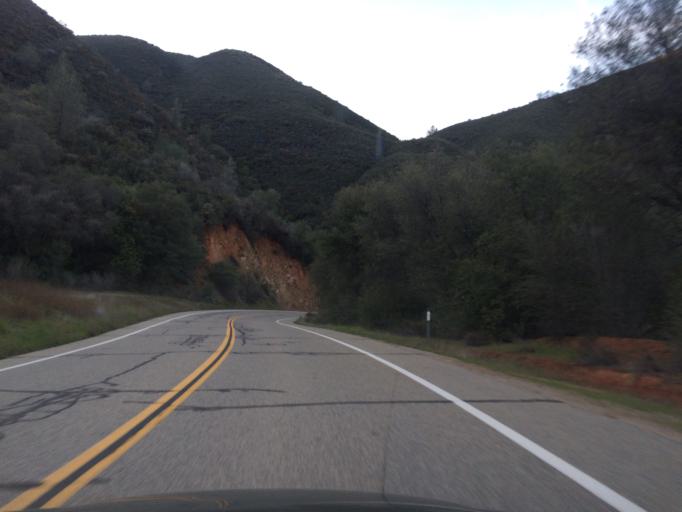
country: US
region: California
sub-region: Mariposa County
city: Midpines
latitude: 37.5899
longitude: -119.9648
